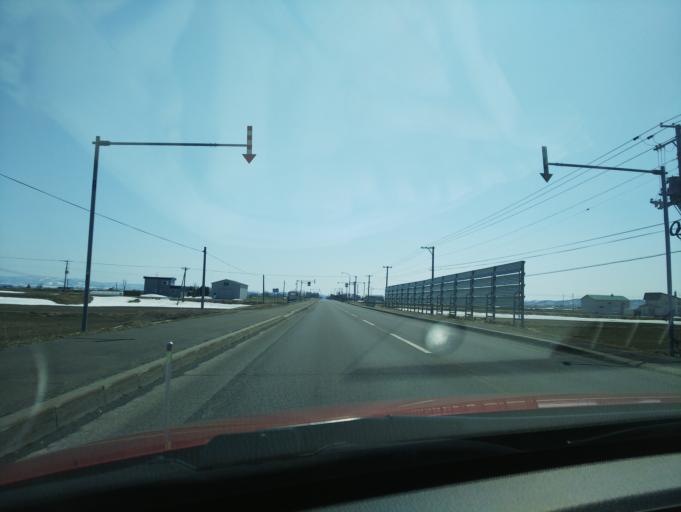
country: JP
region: Hokkaido
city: Nayoro
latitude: 44.2321
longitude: 142.3948
